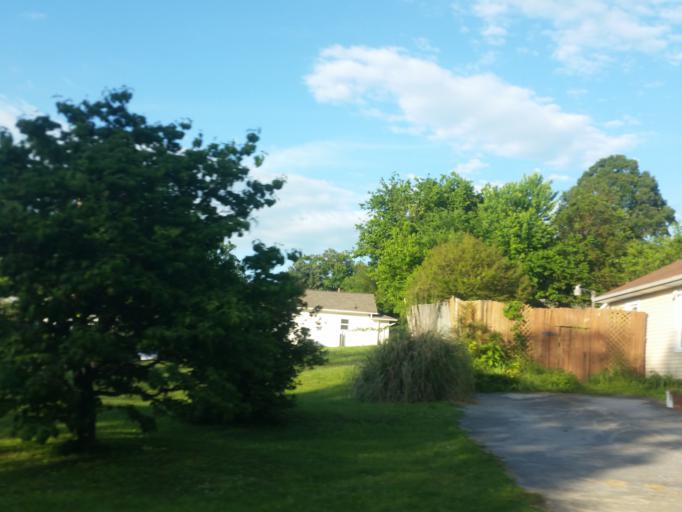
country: US
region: Tennessee
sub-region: Knox County
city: Knoxville
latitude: 35.9946
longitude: -83.9156
